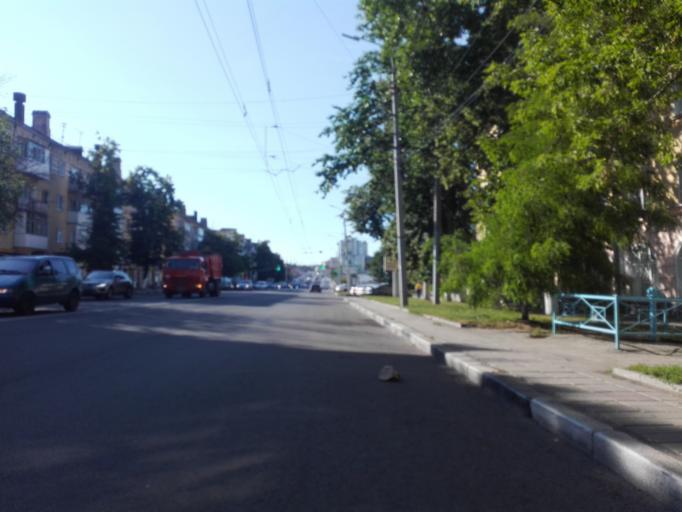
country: RU
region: Orjol
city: Orel
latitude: 52.9721
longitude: 36.0847
